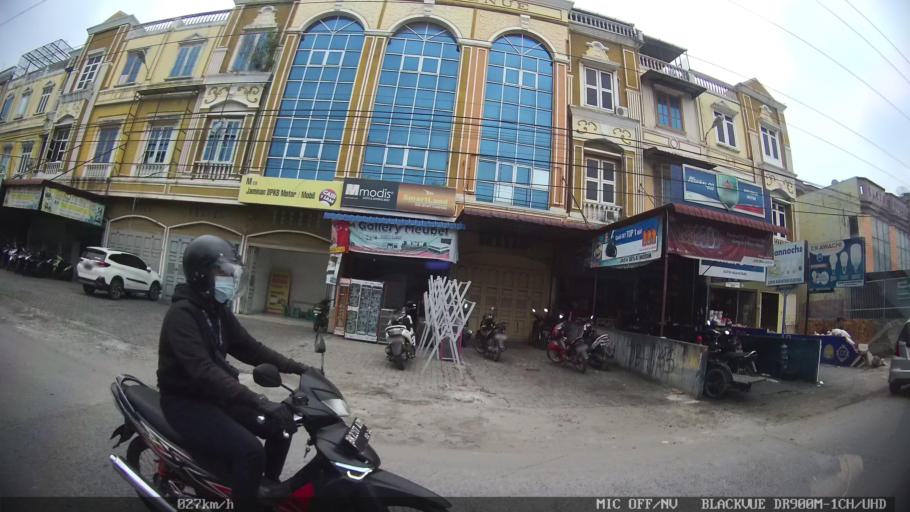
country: ID
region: North Sumatra
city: Medan
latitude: 3.5815
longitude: 98.7198
